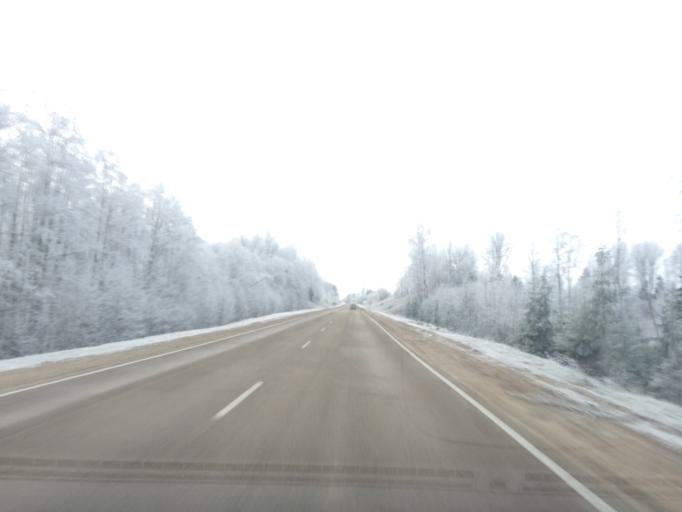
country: LV
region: Rezekne
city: Rezekne
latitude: 56.6064
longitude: 27.4348
